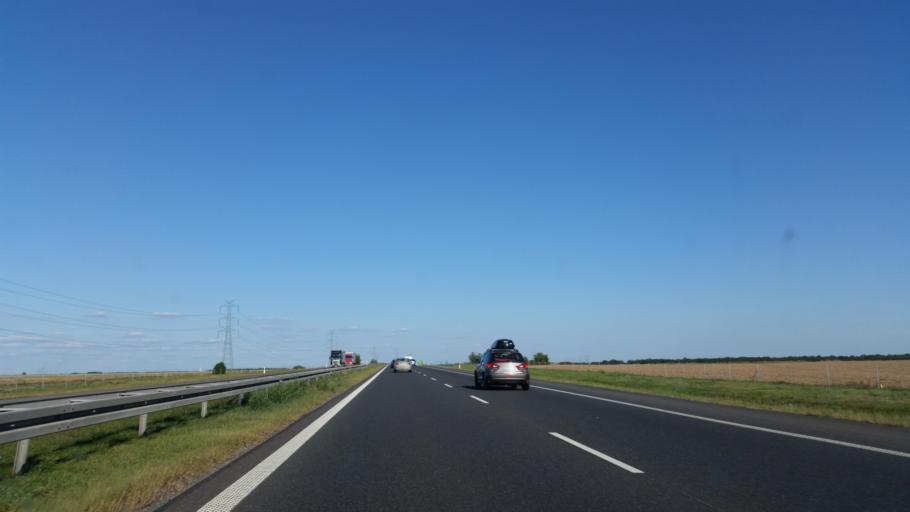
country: PL
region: Opole Voivodeship
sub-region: Powiat brzeski
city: Olszanka
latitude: 50.7366
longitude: 17.4829
